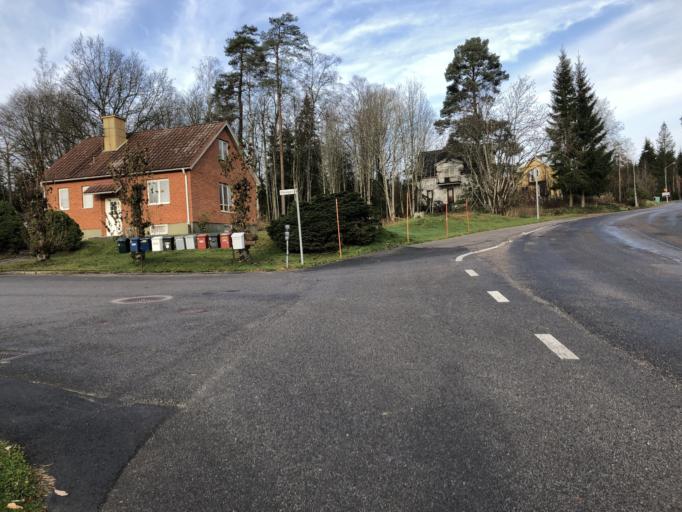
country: SE
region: Vaestra Goetaland
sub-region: Ulricehamns Kommun
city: Ulricehamn
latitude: 57.6968
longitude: 13.5713
